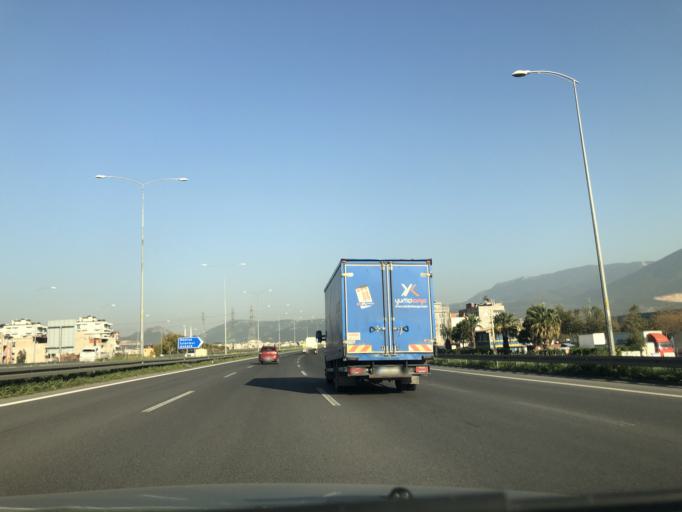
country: TR
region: Izmir
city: Bornova
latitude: 38.4454
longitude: 27.2318
